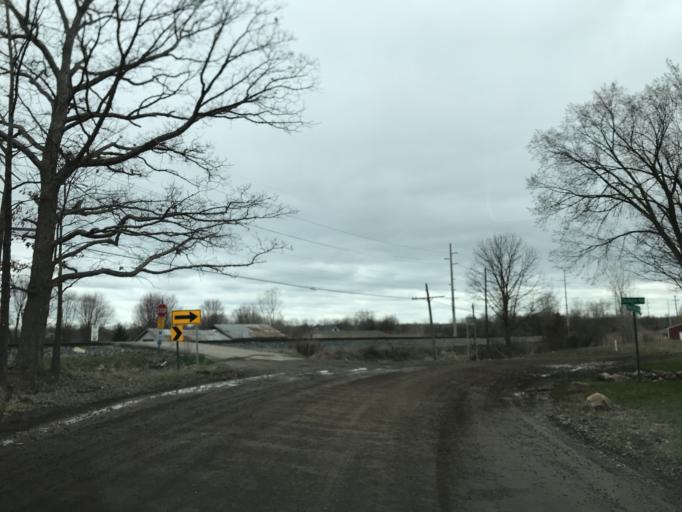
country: US
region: Michigan
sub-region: Oakland County
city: South Lyon
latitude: 42.4745
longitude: -83.6670
